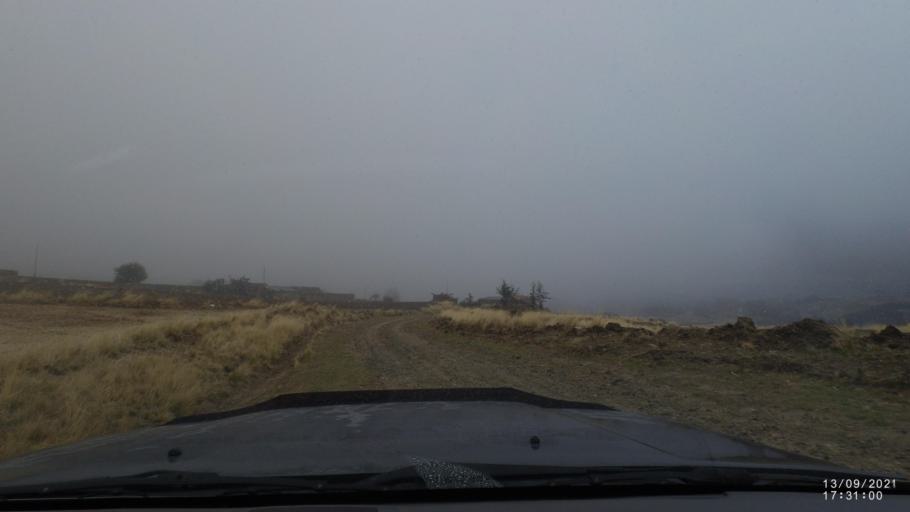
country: BO
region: Cochabamba
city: Colomi
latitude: -17.3608
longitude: -65.7892
